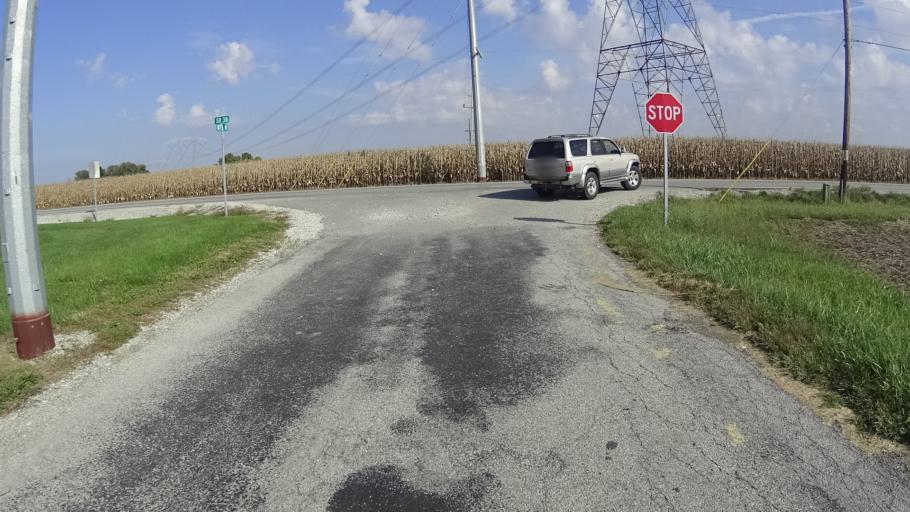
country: US
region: Indiana
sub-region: Madison County
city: Lapel
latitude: 40.0185
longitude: -85.8385
